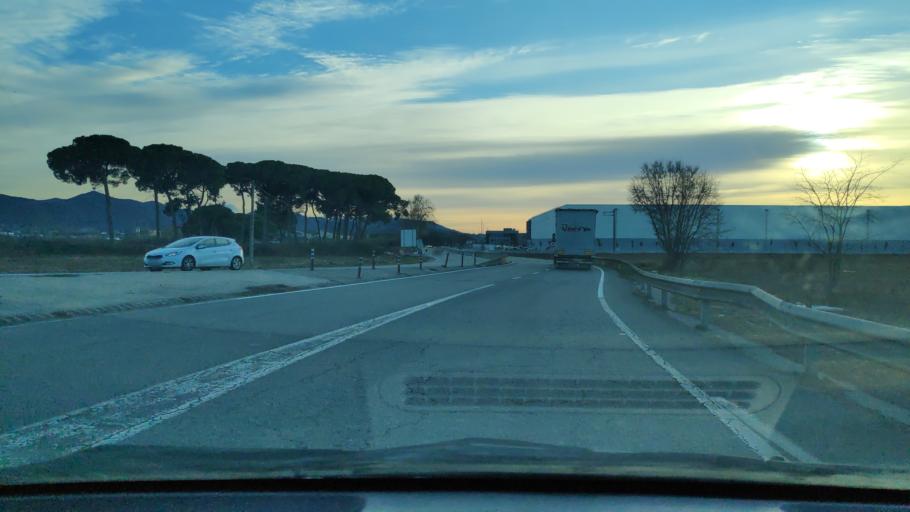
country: ES
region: Catalonia
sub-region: Provincia de Barcelona
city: Llica de Vall
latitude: 41.5747
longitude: 2.2724
